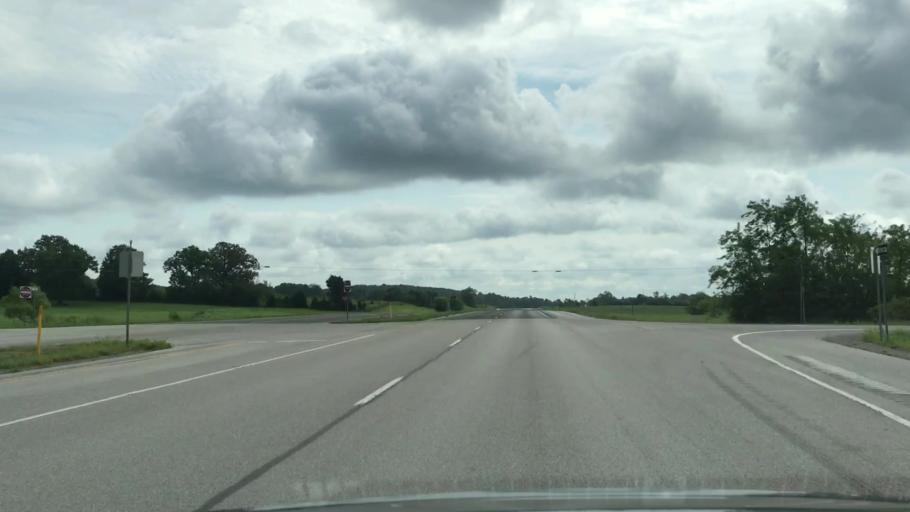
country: US
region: Kentucky
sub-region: Todd County
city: Elkton
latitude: 36.8091
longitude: -87.1303
